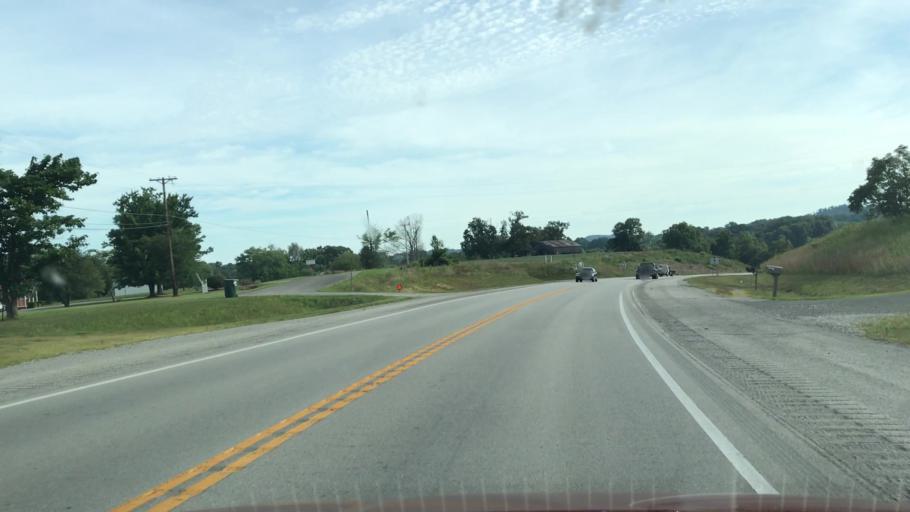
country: US
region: Kentucky
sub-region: Edmonson County
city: Brownsville
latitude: 37.1403
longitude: -86.2303
